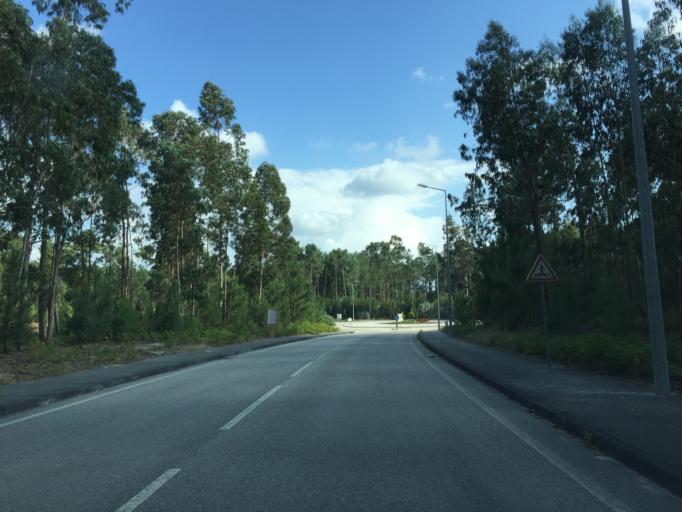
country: PT
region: Leiria
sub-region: Leiria
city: Monte Redondo
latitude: 39.9440
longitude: -8.7984
